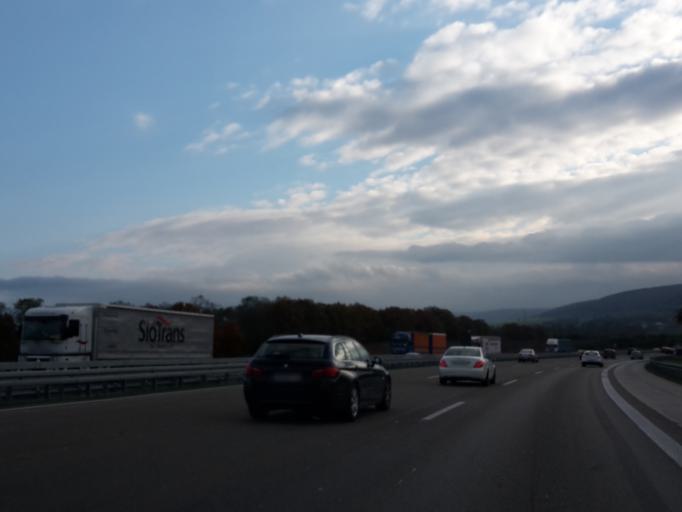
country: DE
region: Hesse
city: Bad Camberg
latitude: 50.2642
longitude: 8.2510
